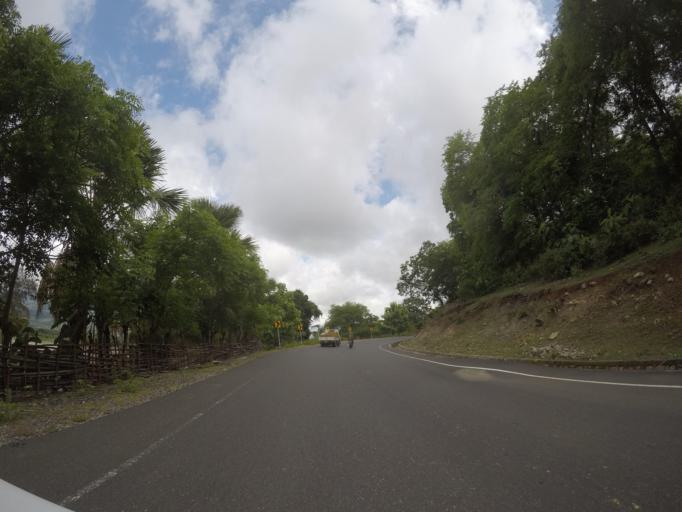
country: TL
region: Liquica
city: Maubara
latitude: -8.7431
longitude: 125.1220
